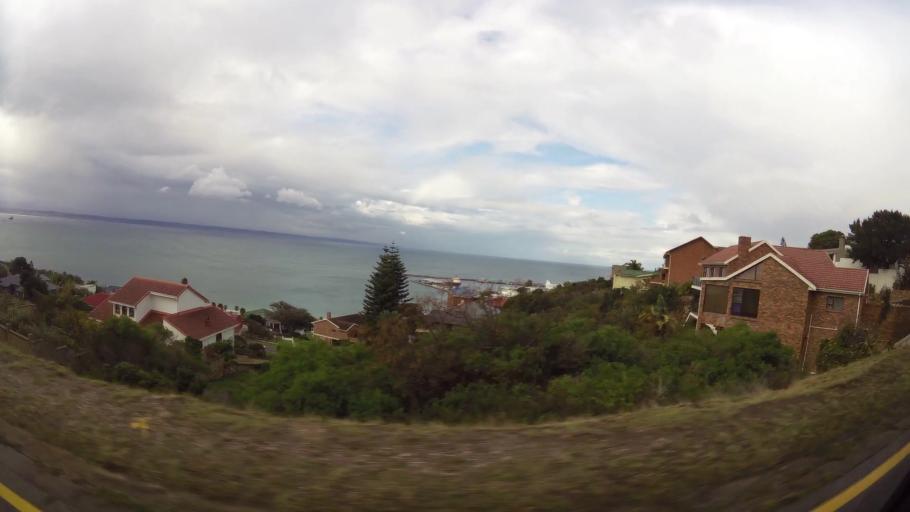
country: ZA
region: Western Cape
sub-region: Eden District Municipality
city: Mossel Bay
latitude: -34.1806
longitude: 22.1335
